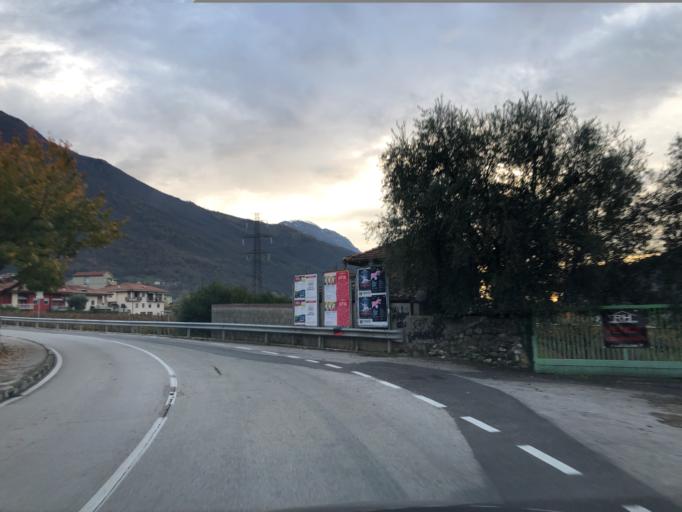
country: IT
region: Trentino-Alto Adige
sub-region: Provincia di Trento
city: Bolognano-Vignole
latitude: 45.9155
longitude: 10.9007
